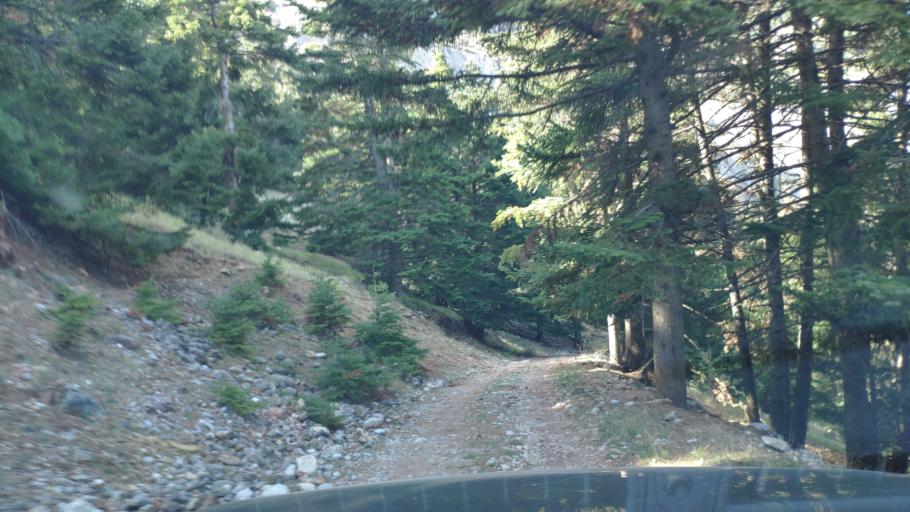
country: GR
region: West Greece
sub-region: Nomos Achaias
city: Aiyira
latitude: 37.9810
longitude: 22.3443
